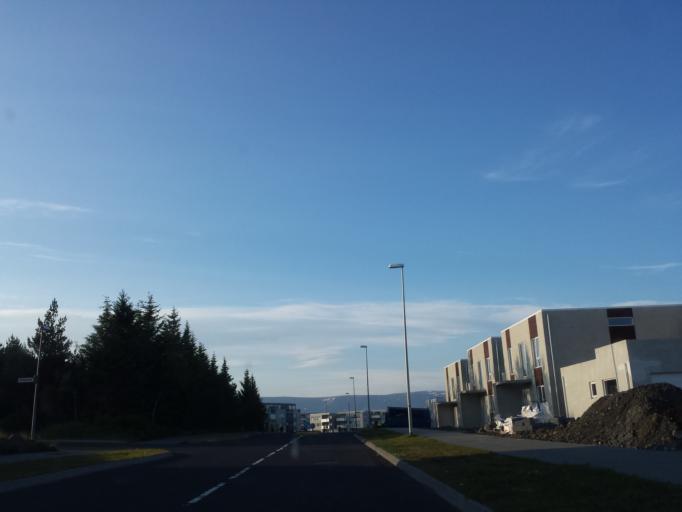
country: IS
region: Capital Region
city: Mosfellsbaer
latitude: 64.0960
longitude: -21.7781
